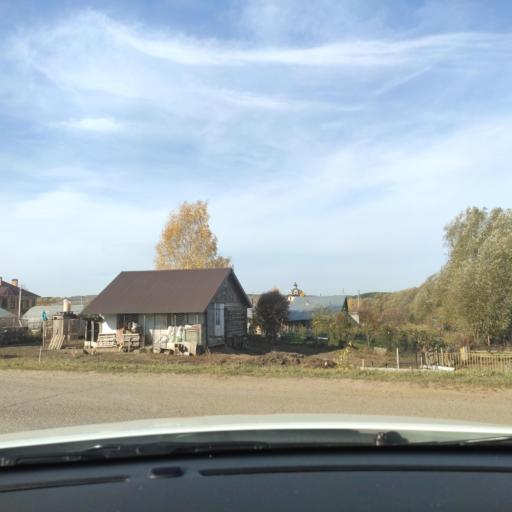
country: RU
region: Tatarstan
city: Vysokaya Gora
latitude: 55.7486
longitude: 49.4061
